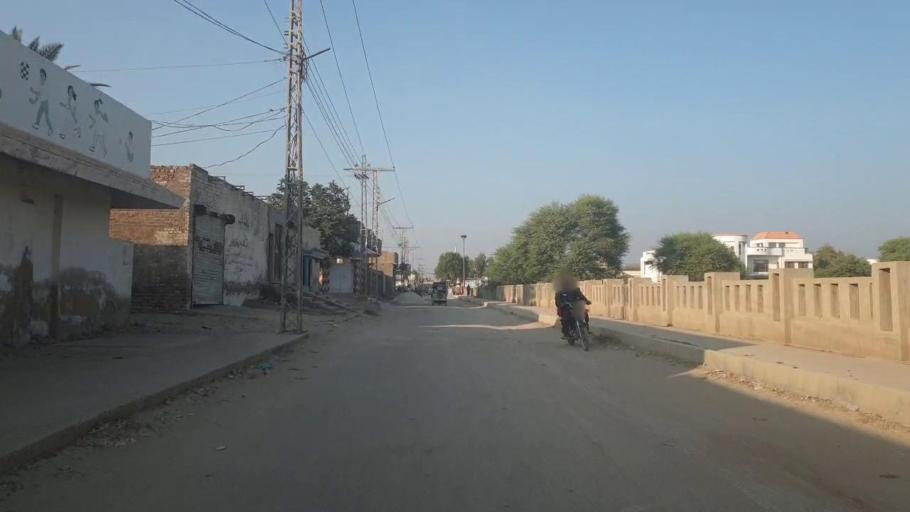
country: PK
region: Sindh
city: Jamshoro
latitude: 25.4377
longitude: 68.2905
